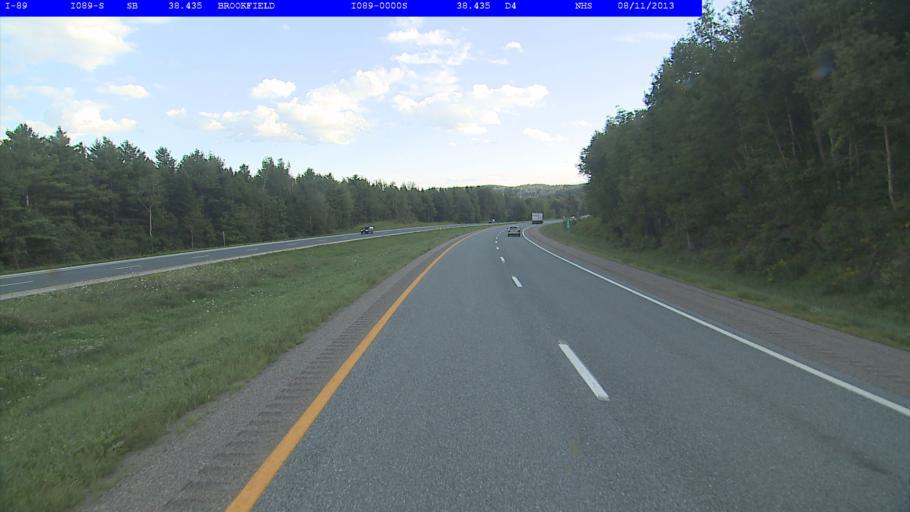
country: US
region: Vermont
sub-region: Orange County
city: Williamstown
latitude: 44.0517
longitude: -72.6051
